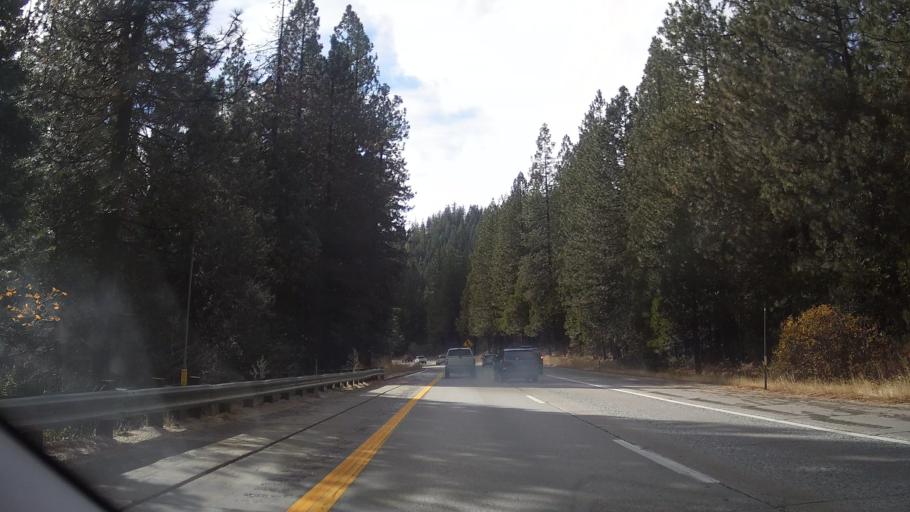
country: US
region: California
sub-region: Placer County
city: Foresthill
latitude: 39.2441
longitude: -120.7490
